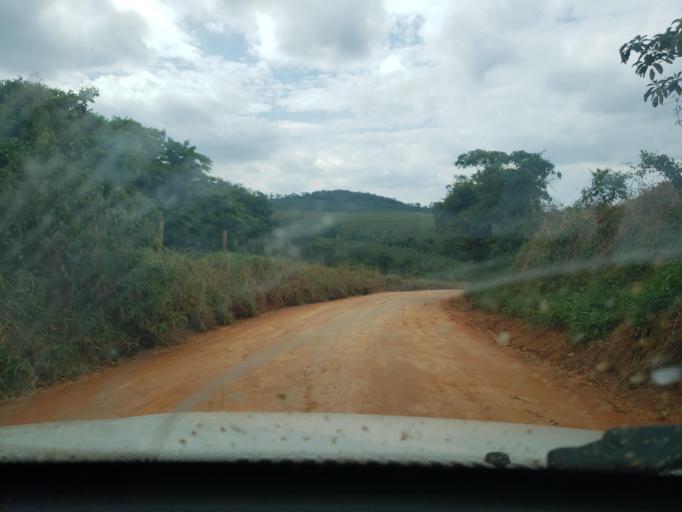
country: BR
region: Minas Gerais
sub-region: Boa Esperanca
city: Boa Esperanca
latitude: -20.9786
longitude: -45.6000
